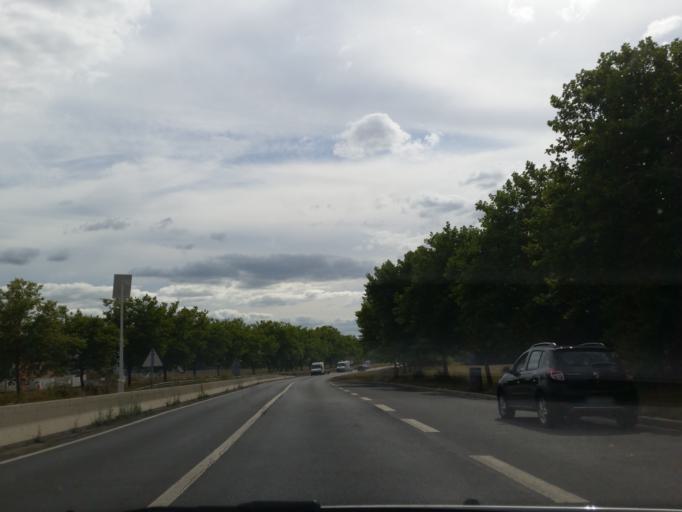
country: FR
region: Centre
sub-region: Departement du Loir-et-Cher
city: La Chaussee-Saint-Victor
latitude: 47.6167
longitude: 1.3464
